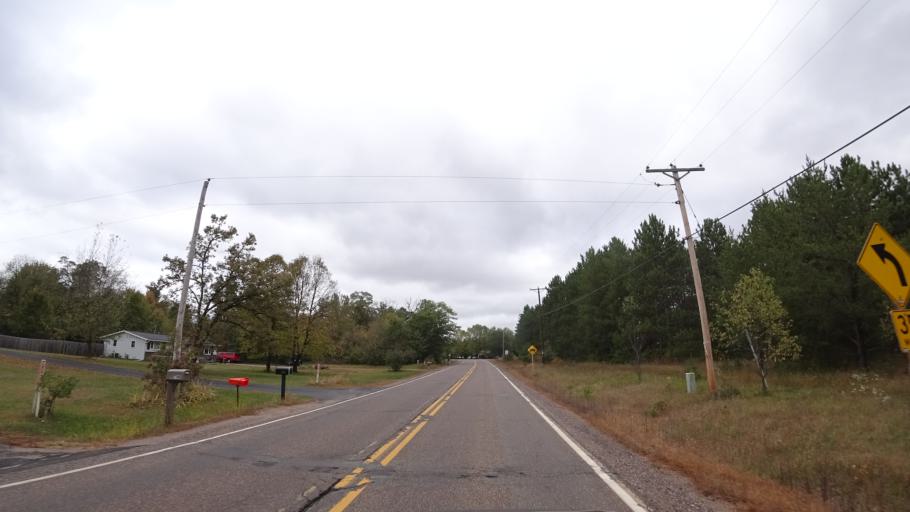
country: US
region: Wisconsin
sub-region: Chippewa County
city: Lake Wissota
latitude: 44.9467
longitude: -91.2628
